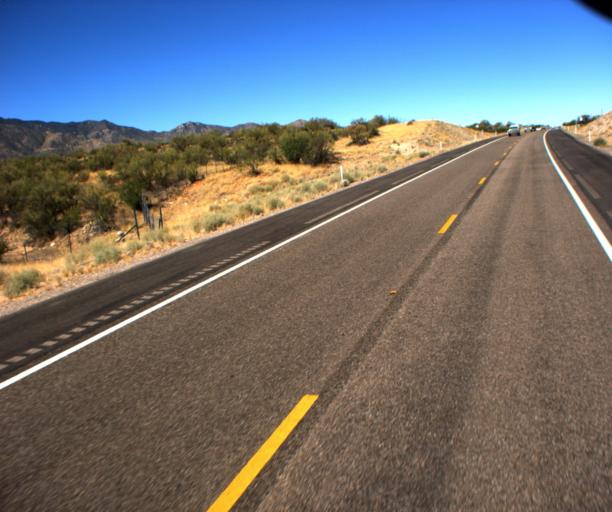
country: US
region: Arizona
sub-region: Pima County
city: Three Points
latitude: 32.0292
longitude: -111.5661
